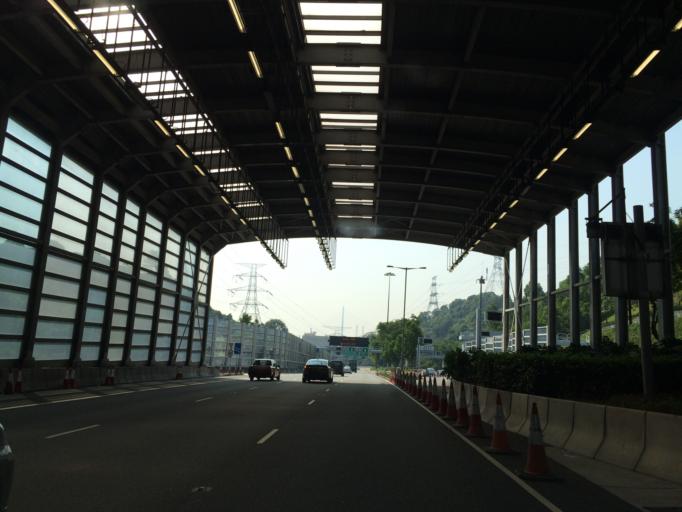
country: HK
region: Sham Shui Po
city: Sham Shui Po
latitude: 22.3456
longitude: 114.1469
